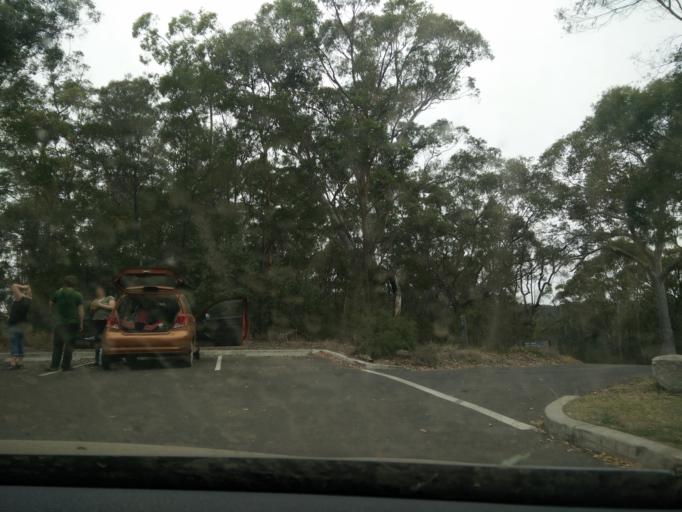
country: AU
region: New South Wales
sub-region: Blue Mountains Municipality
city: Glenbrook
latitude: -33.7784
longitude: 150.6204
